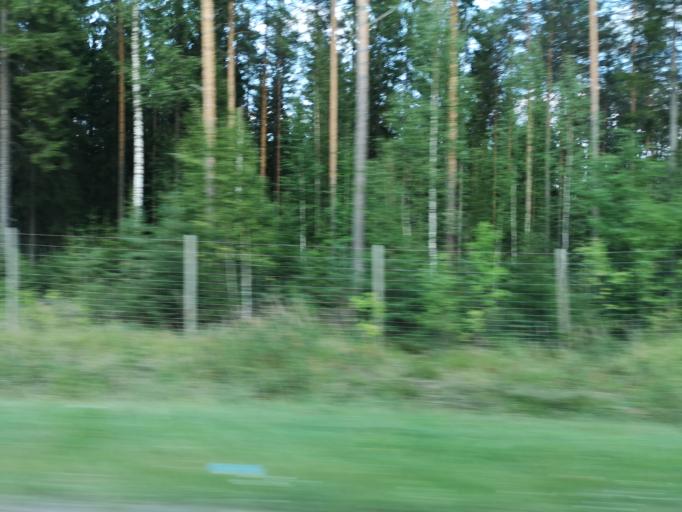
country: FI
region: Paijanne Tavastia
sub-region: Lahti
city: Hartola
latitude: 61.5307
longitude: 26.0068
